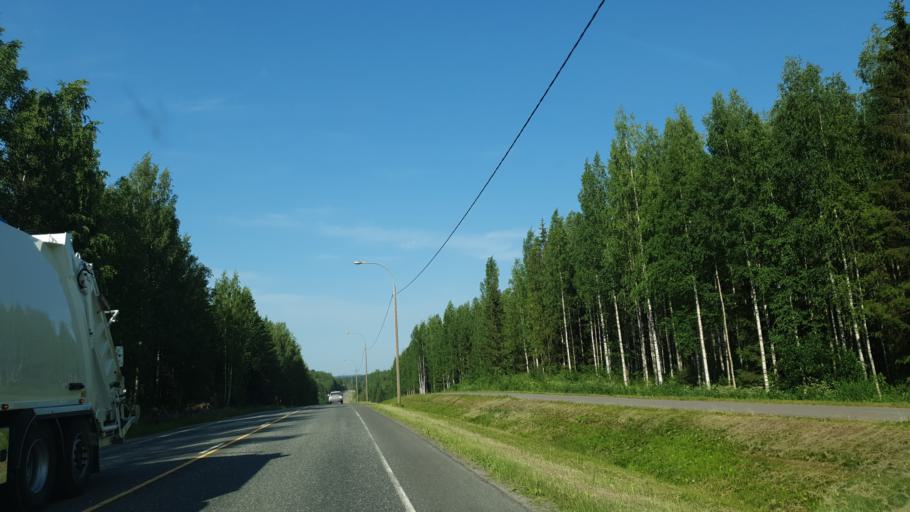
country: FI
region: Northern Savo
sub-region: Kuopio
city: Siilinjaervi
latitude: 63.1079
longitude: 27.7523
